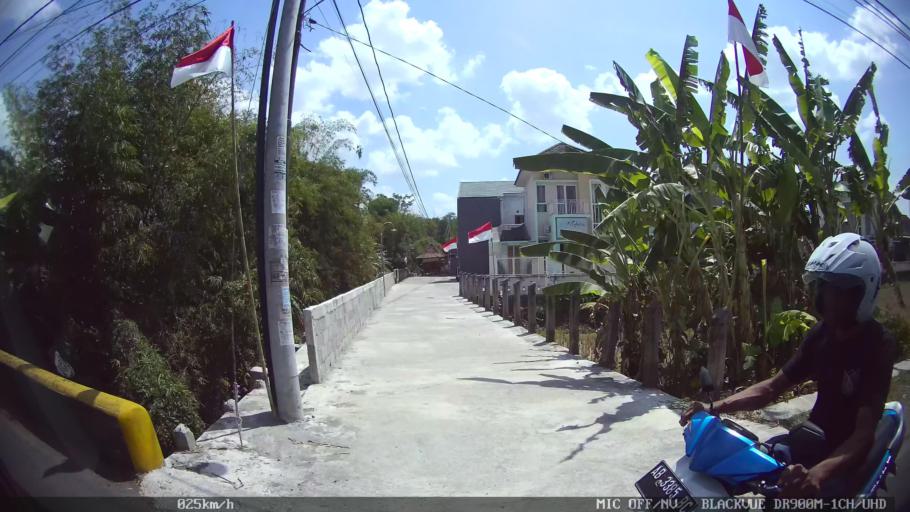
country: ID
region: Daerah Istimewa Yogyakarta
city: Sewon
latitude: -7.8433
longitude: 110.3877
